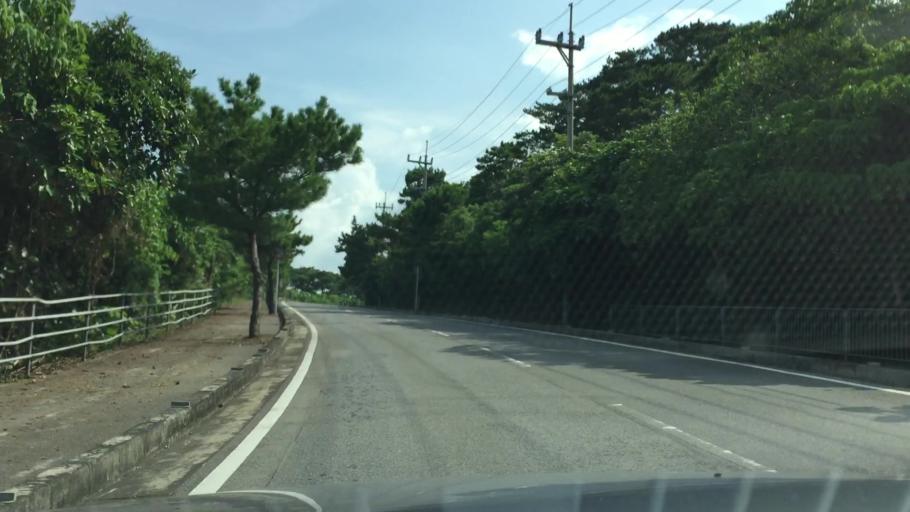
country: JP
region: Okinawa
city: Ishigaki
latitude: 24.4860
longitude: 124.2706
